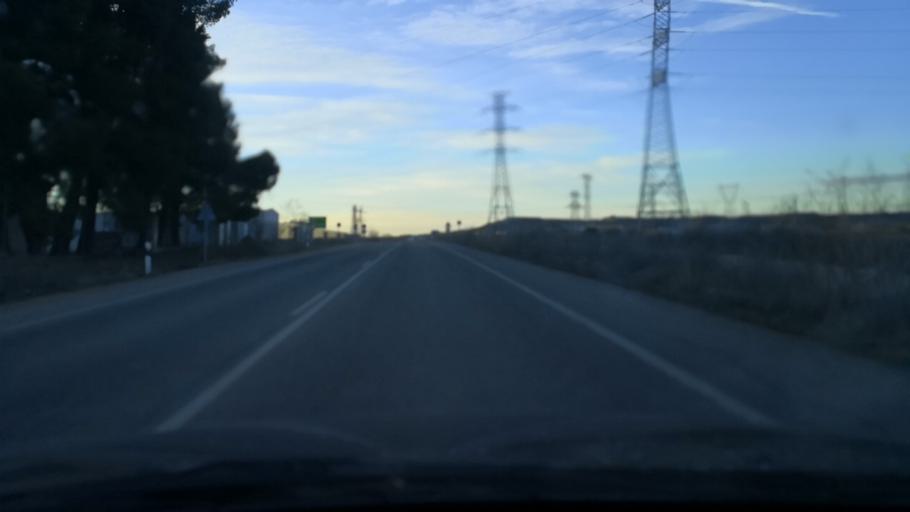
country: ES
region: Castille and Leon
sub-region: Provincia de Valladolid
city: Tordesillas
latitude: 41.5068
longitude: -5.0104
